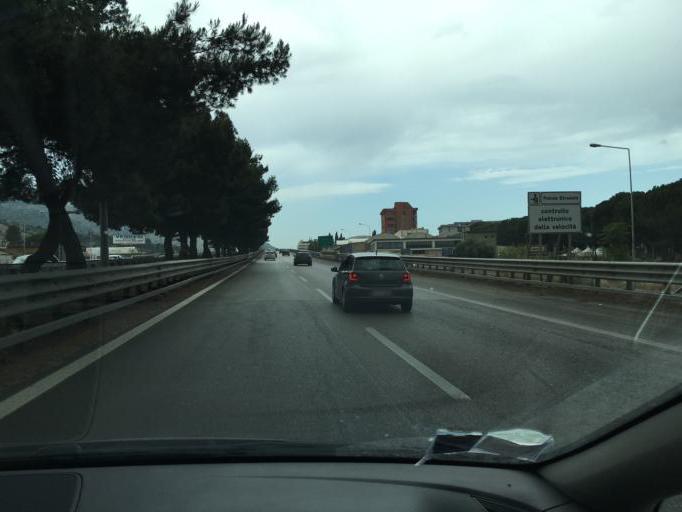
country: IT
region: Sicily
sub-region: Palermo
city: Palermo
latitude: 38.1530
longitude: 13.3211
